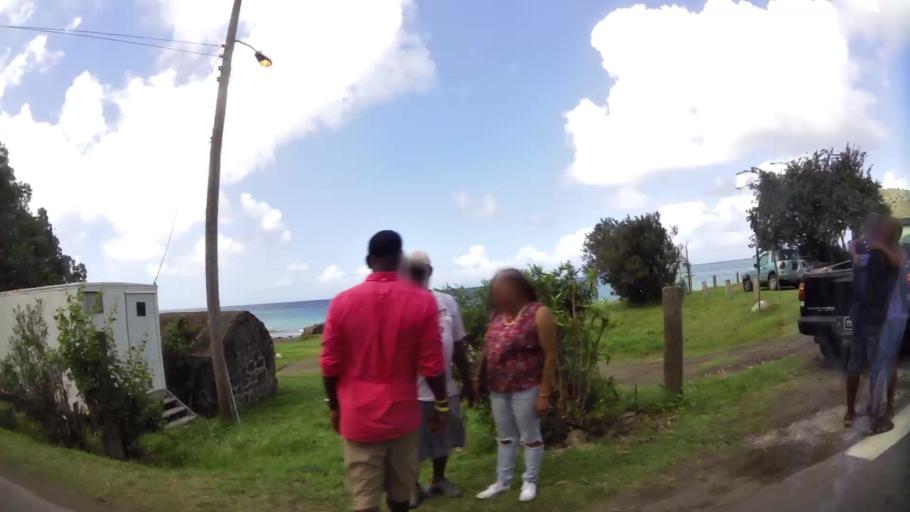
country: MS
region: Saint Peter
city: Brades
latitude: 16.7962
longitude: -62.2090
